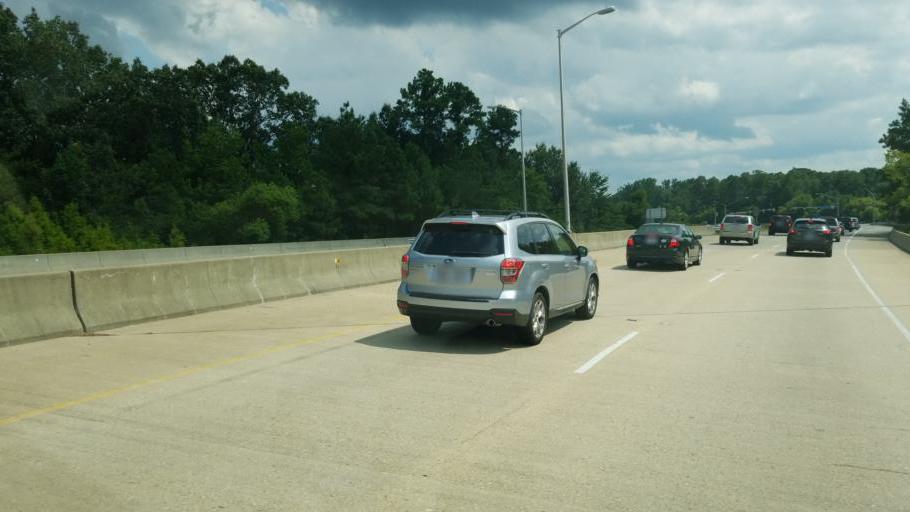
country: US
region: North Carolina
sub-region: Currituck County
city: Moyock
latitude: 36.5660
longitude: -76.1994
